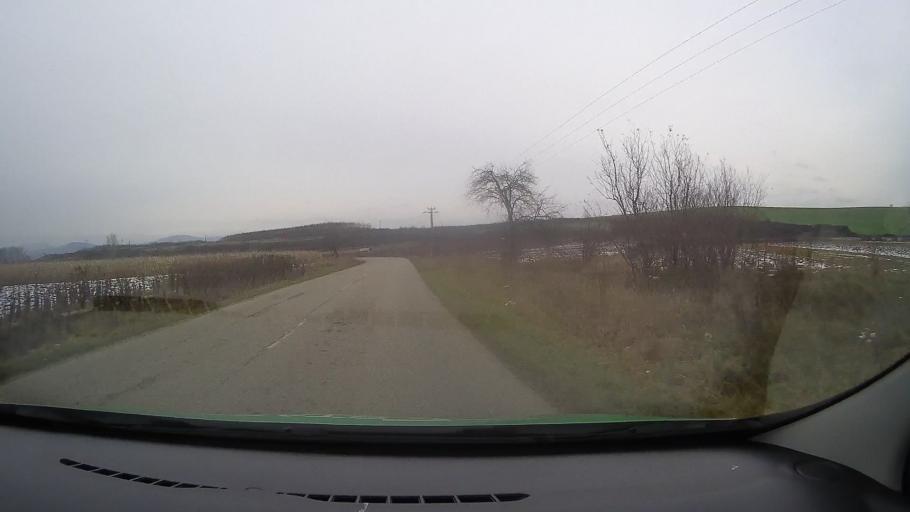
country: RO
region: Hunedoara
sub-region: Comuna Romos
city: Romos
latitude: 45.8621
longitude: 23.2734
